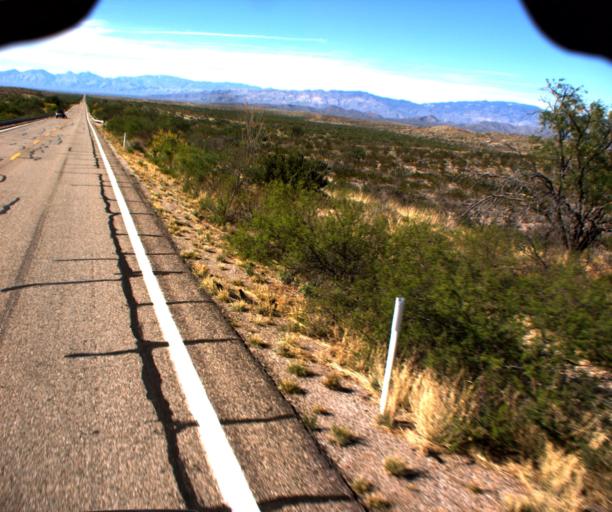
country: US
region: Arizona
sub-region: Pima County
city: Corona de Tucson
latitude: 31.9332
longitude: -110.6597
